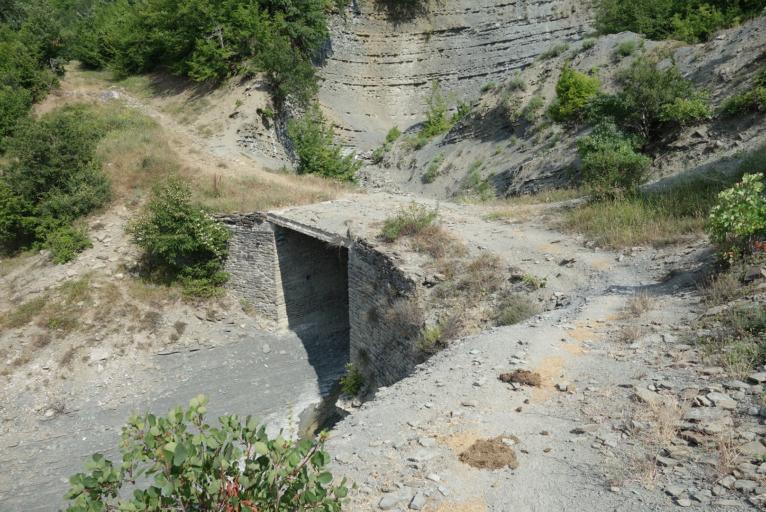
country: AL
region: Gjirokaster
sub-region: Rrethi i Permetit
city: Frasher
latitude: 40.3781
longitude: 20.4029
